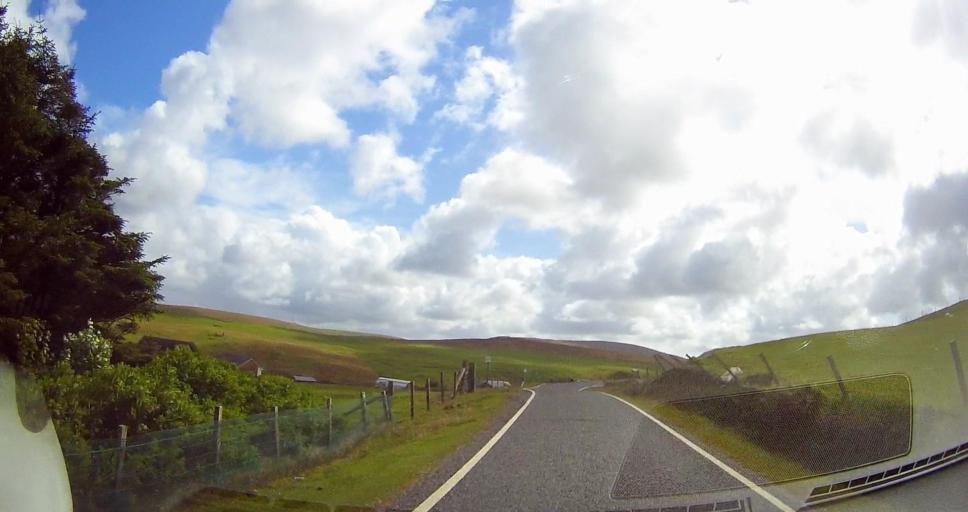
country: GB
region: Scotland
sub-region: Shetland Islands
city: Lerwick
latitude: 60.5315
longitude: -1.3621
